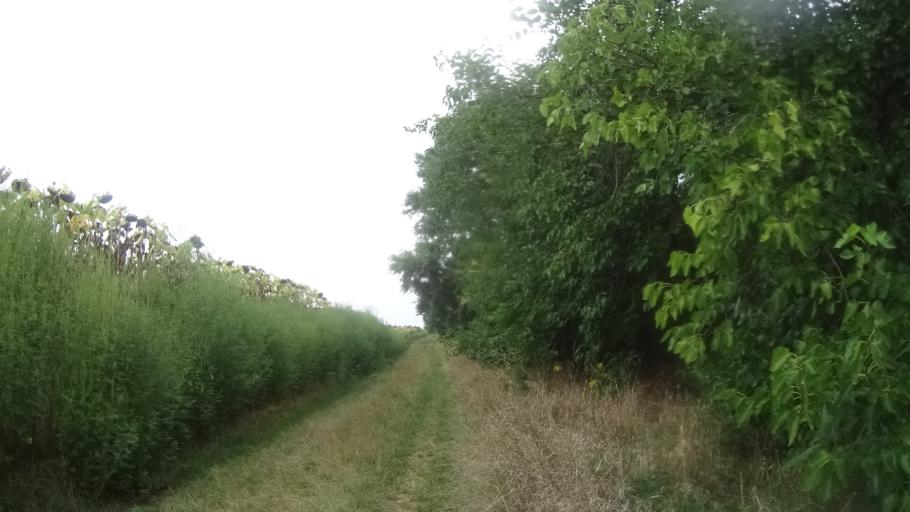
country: SK
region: Nitriansky
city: Komarno
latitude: 47.7608
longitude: 18.0871
